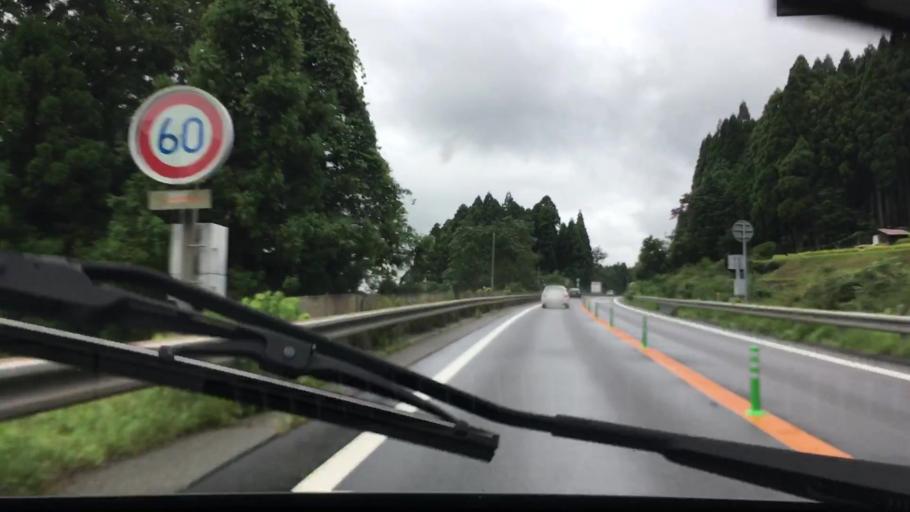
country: JP
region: Hyogo
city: Nishiwaki
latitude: 35.1143
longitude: 134.7839
